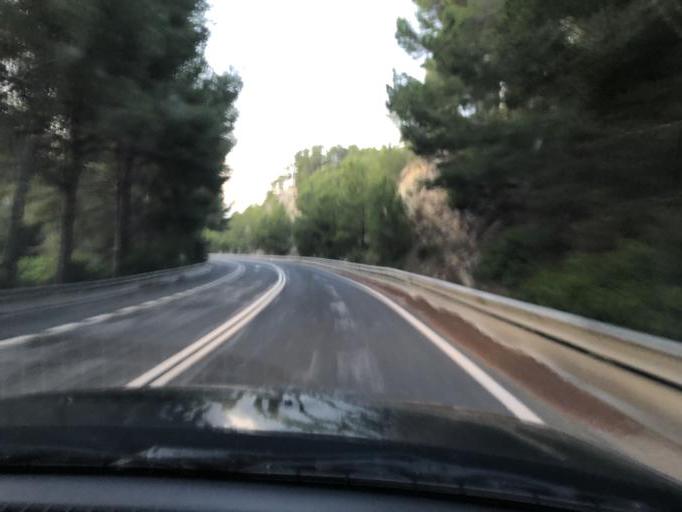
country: ES
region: Balearic Islands
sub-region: Illes Balears
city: Andratx
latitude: 39.5583
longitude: 2.4198
